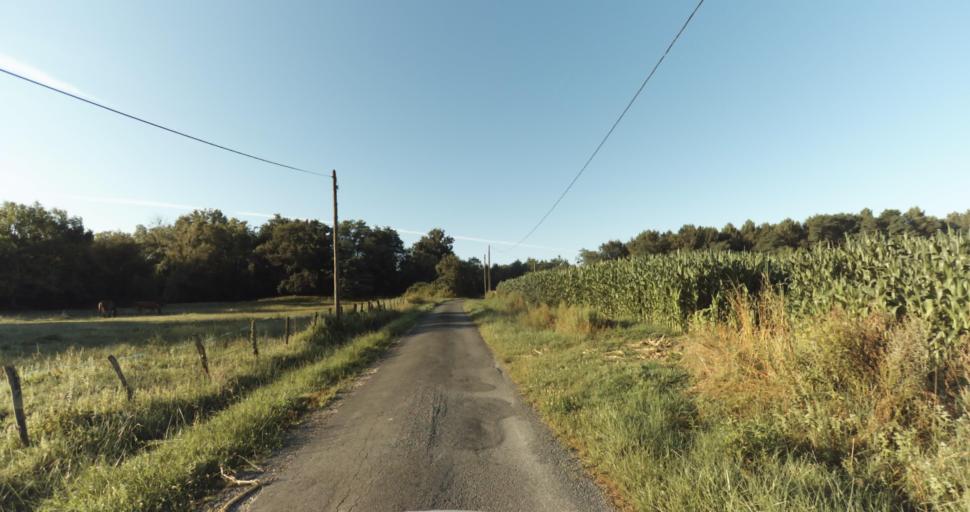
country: FR
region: Aquitaine
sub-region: Departement de la Gironde
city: Bazas
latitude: 44.4167
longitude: -0.2333
